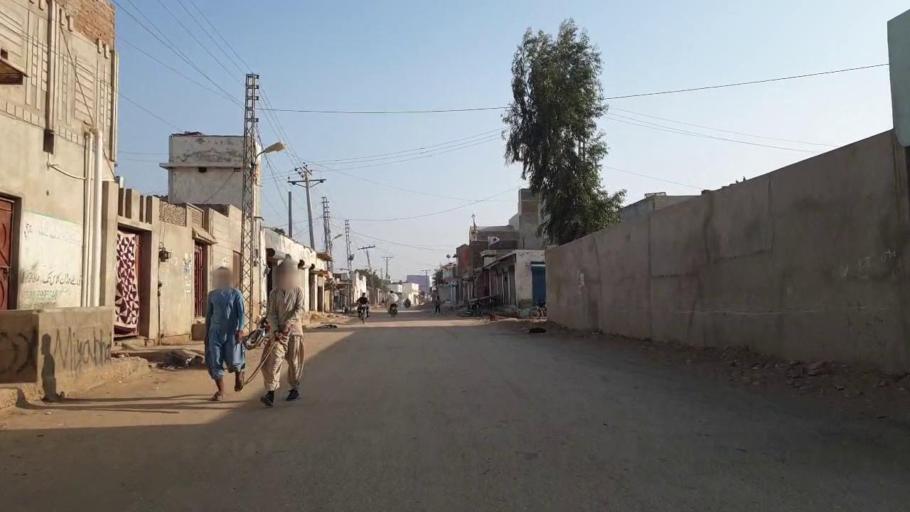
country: PK
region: Sindh
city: Kotri
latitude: 25.3592
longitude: 68.2618
